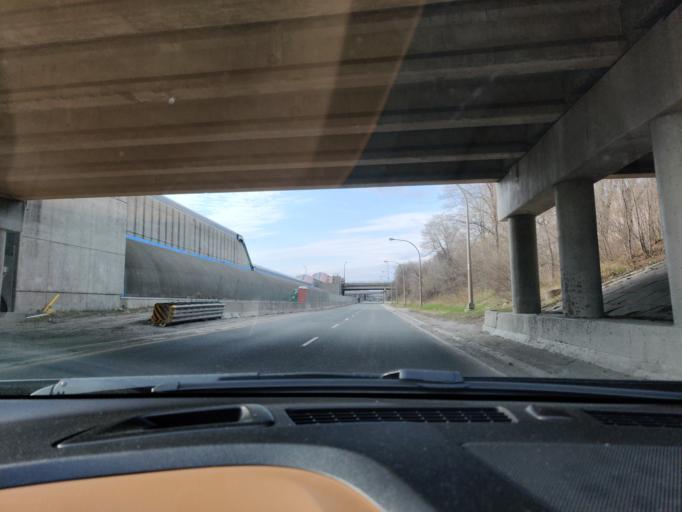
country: CA
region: Ontario
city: Toronto
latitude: 43.7078
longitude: -79.4398
